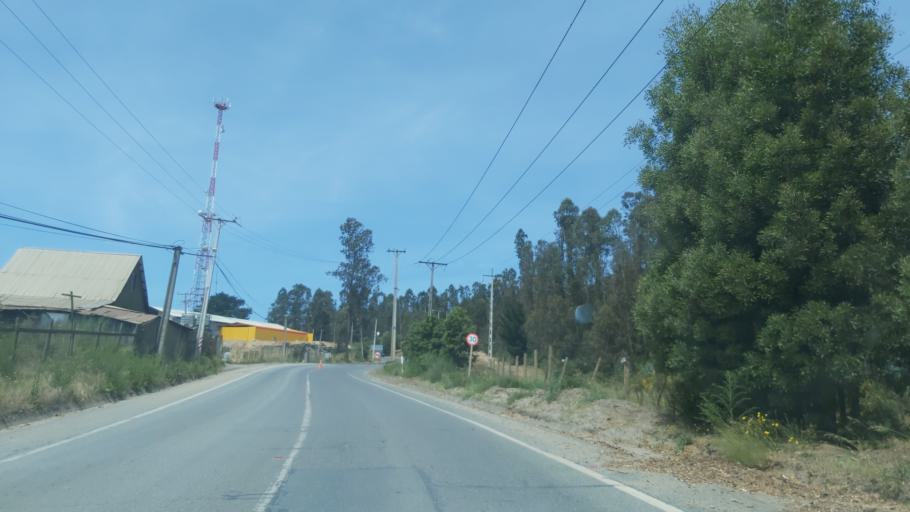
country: CL
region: Maule
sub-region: Provincia de Talca
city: Constitucion
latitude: -35.3675
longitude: -72.4053
